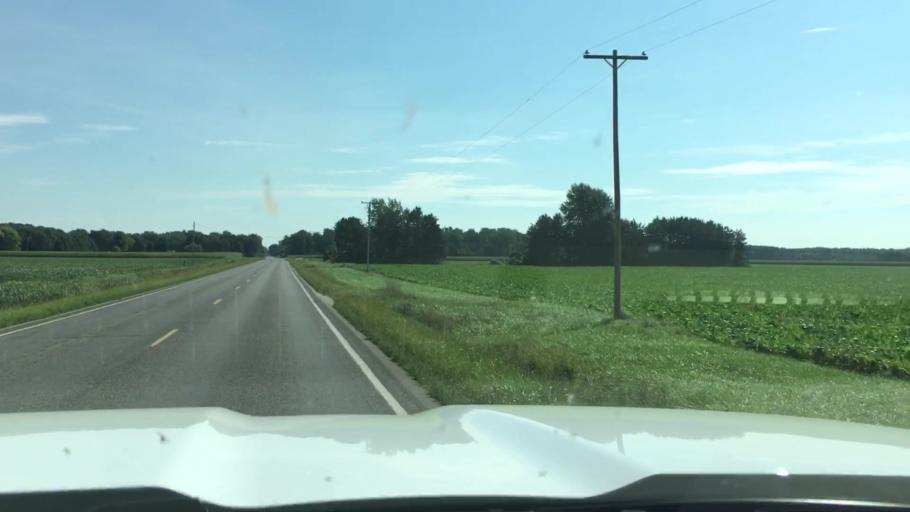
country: US
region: Michigan
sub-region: Saginaw County
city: Freeland
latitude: 43.5244
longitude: -84.1755
